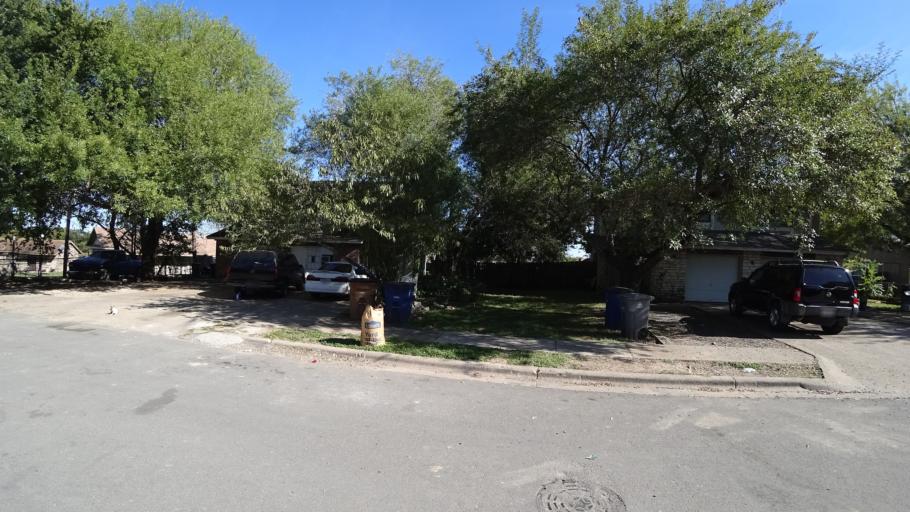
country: US
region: Texas
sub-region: Travis County
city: Austin
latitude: 30.1962
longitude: -97.7397
